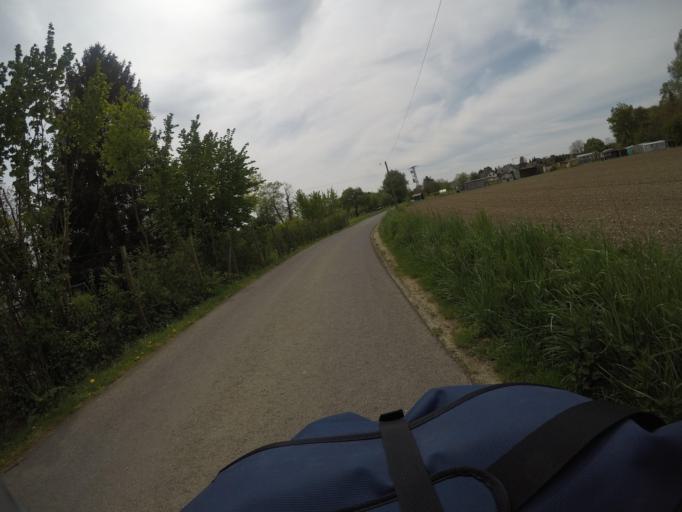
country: DE
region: Baden-Wuerttemberg
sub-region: Freiburg Region
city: Kehl
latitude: 48.6045
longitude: 7.8469
